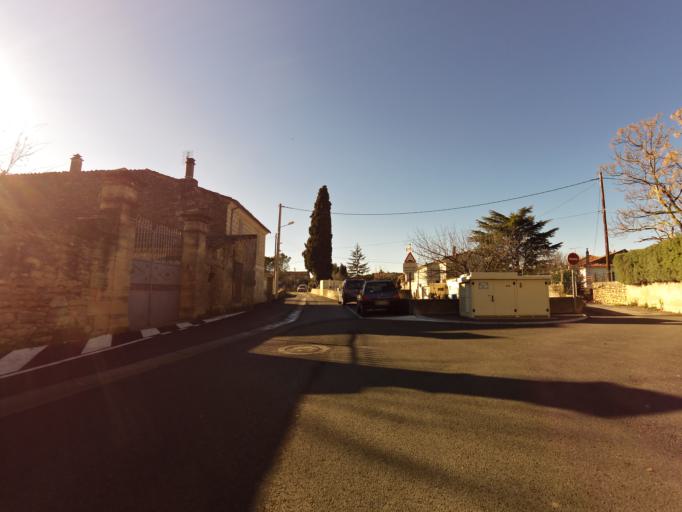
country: FR
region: Languedoc-Roussillon
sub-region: Departement du Gard
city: Aigues-Vives
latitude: 43.7404
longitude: 4.1696
